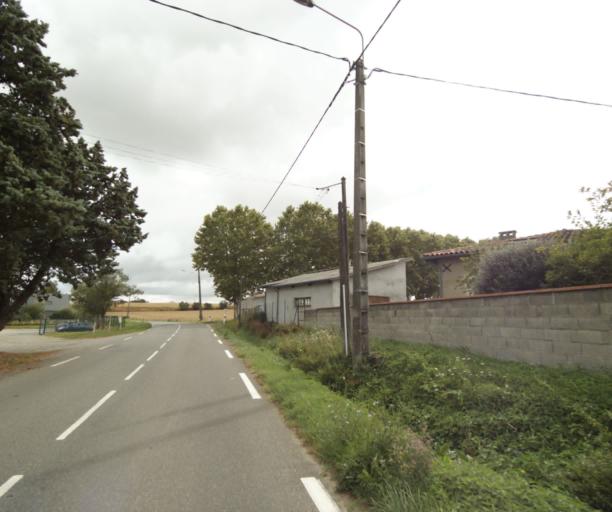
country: FR
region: Midi-Pyrenees
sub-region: Departement de la Haute-Garonne
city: Flourens
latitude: 43.5968
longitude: 1.5463
